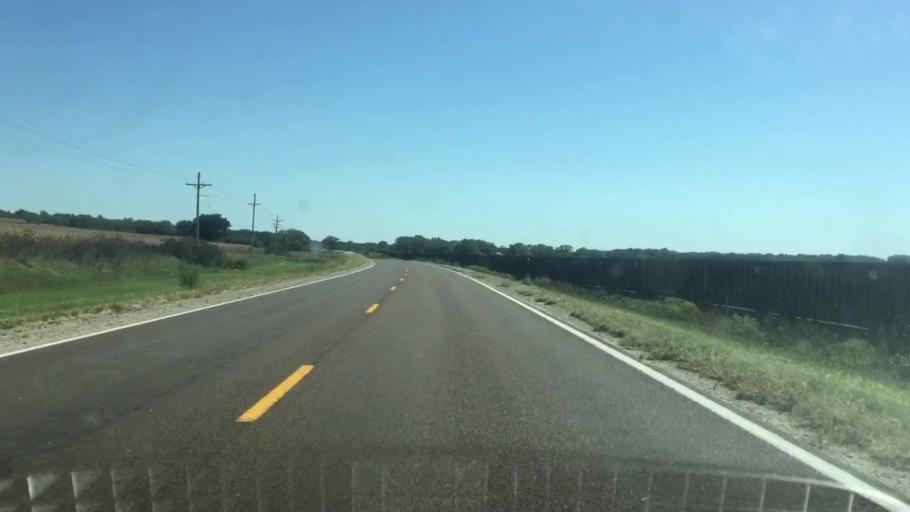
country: US
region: Nebraska
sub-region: Jefferson County
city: Fairbury
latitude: 40.0857
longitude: -97.1163
